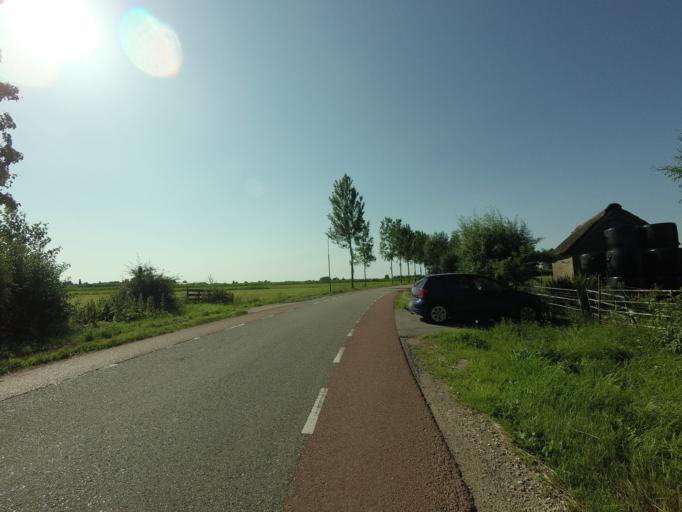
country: NL
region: Utrecht
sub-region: Gemeente IJsselstein
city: IJsselstein
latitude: 52.0560
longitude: 5.0216
